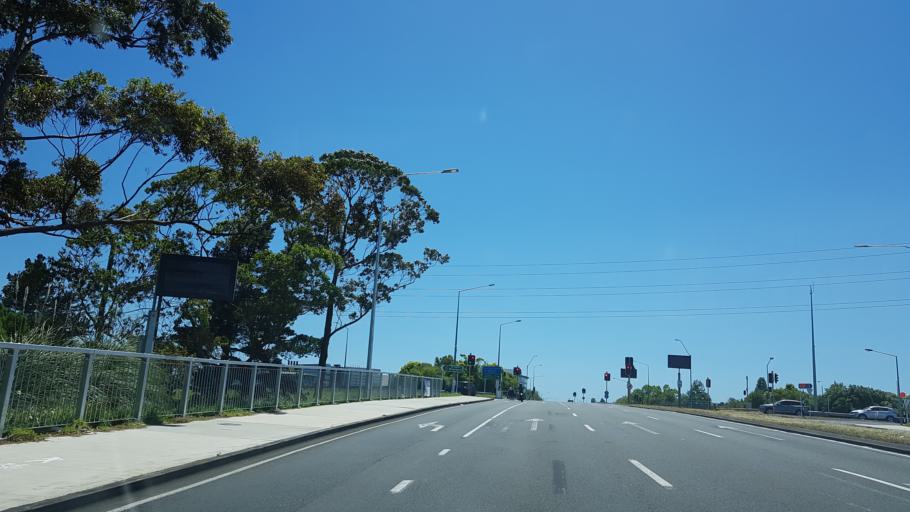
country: NZ
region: Auckland
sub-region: Auckland
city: North Shore
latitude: -36.7891
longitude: 174.7515
